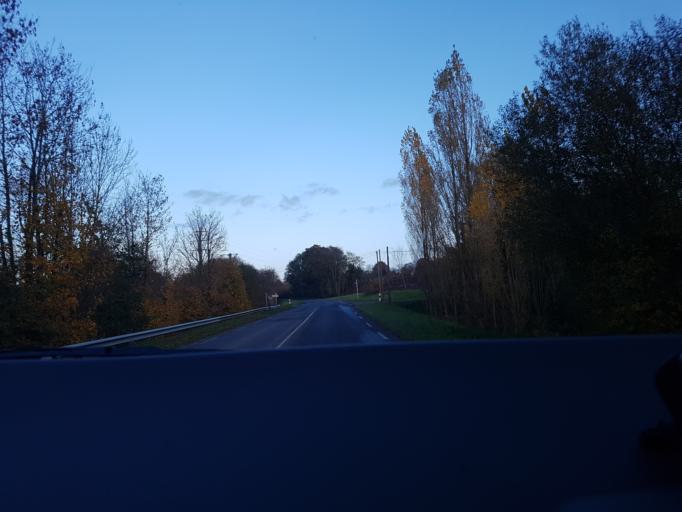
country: FR
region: Lower Normandy
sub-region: Departement du Calvados
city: Dozule
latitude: 49.2492
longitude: 0.0013
